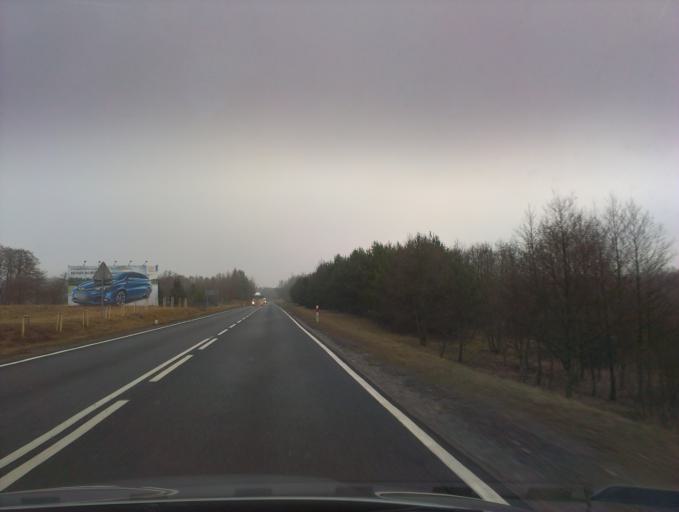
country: PL
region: West Pomeranian Voivodeship
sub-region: Powiat koszalinski
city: Bobolice
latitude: 53.9775
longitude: 16.5492
